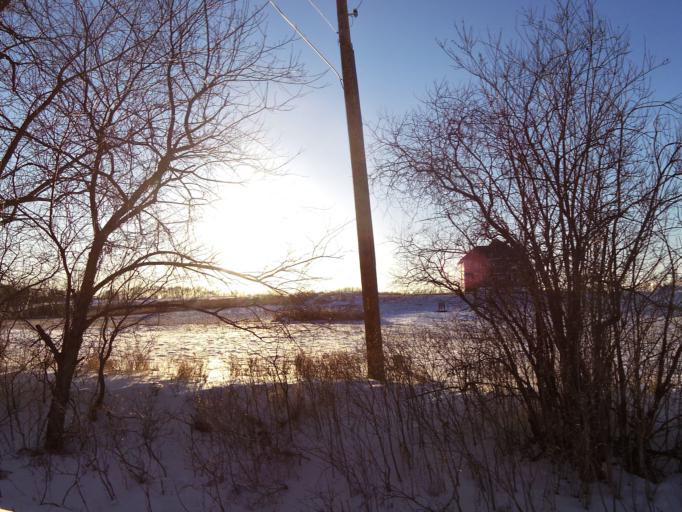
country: US
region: Minnesota
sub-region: Washington County
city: Lake Elmo
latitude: 44.9887
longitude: -92.8431
